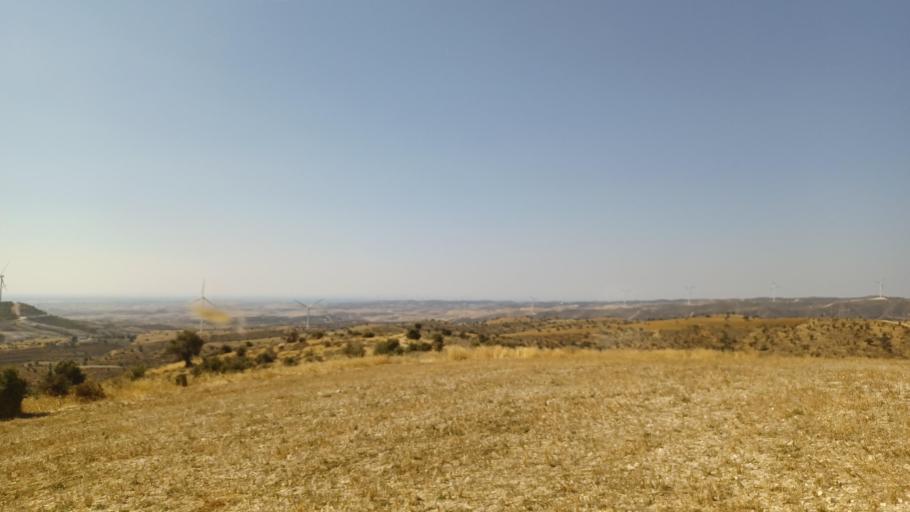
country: CY
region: Larnaka
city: Psevdas
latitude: 34.9685
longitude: 33.4848
